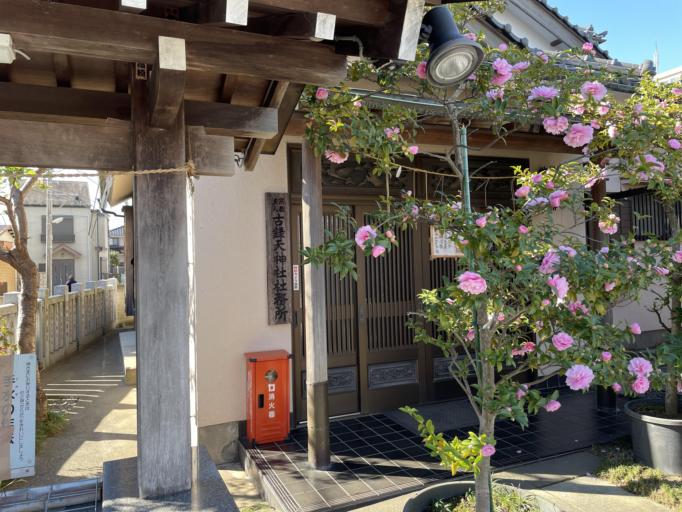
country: JP
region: Chiba
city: Matsudo
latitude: 35.7586
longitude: 139.8701
